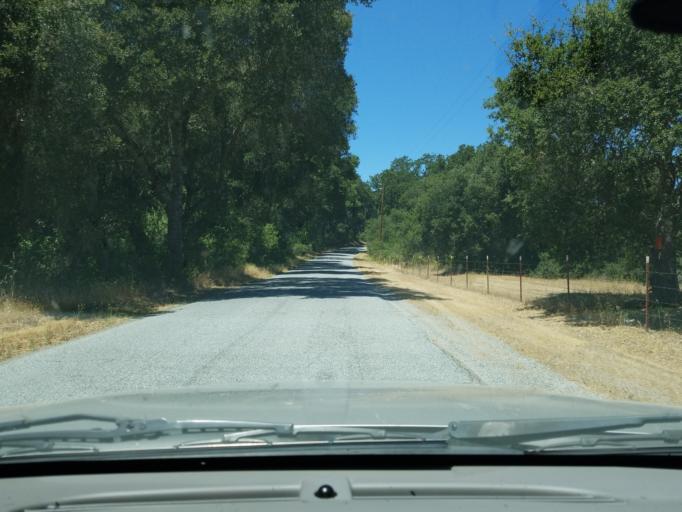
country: US
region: California
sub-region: Monterey County
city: Gonzales
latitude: 36.3788
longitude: -121.5671
